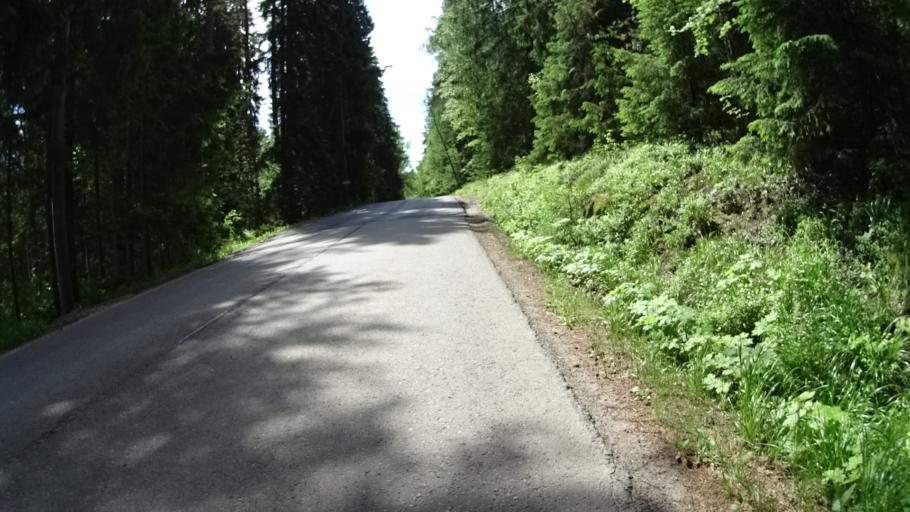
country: FI
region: Uusimaa
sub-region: Helsinki
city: Espoo
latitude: 60.2570
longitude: 24.6529
